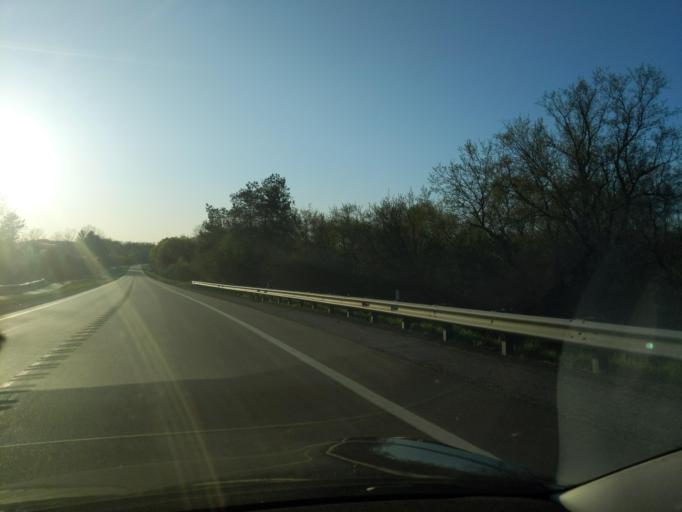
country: US
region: Michigan
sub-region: Washtenaw County
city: Chelsea
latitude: 42.3482
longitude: -84.0446
